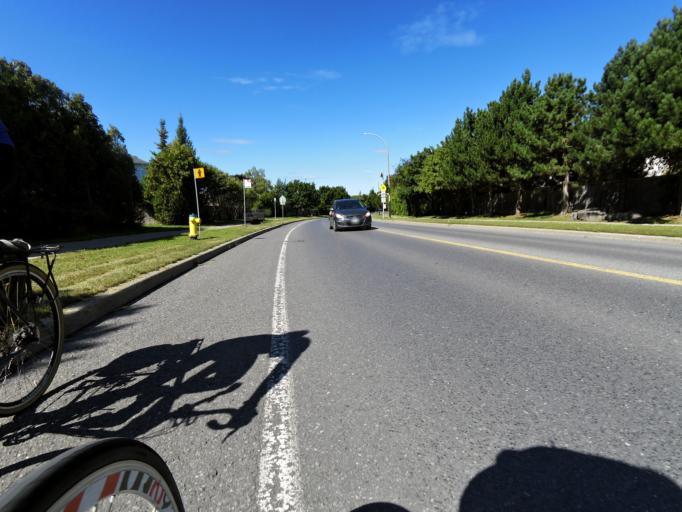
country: CA
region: Ontario
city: Bells Corners
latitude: 45.2808
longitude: -75.8422
